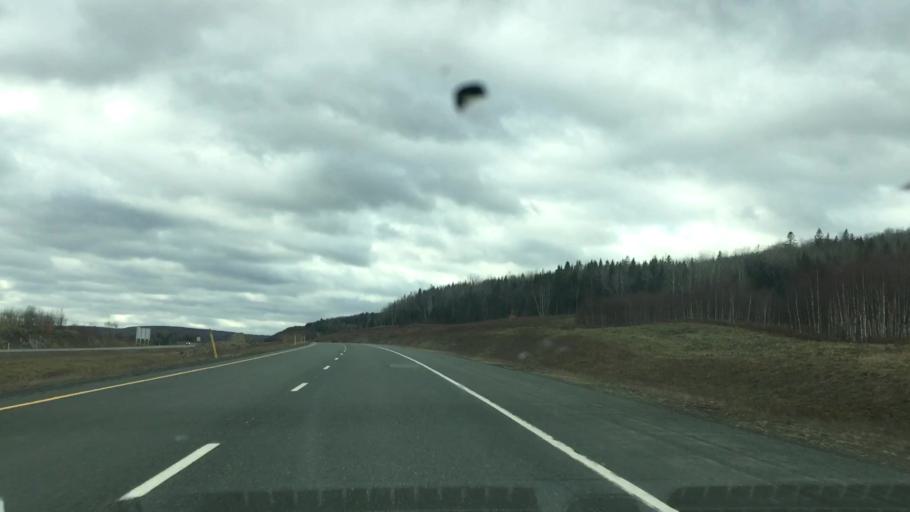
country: US
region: Maine
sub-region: Aroostook County
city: Fort Fairfield
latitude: 46.7265
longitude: -67.7278
